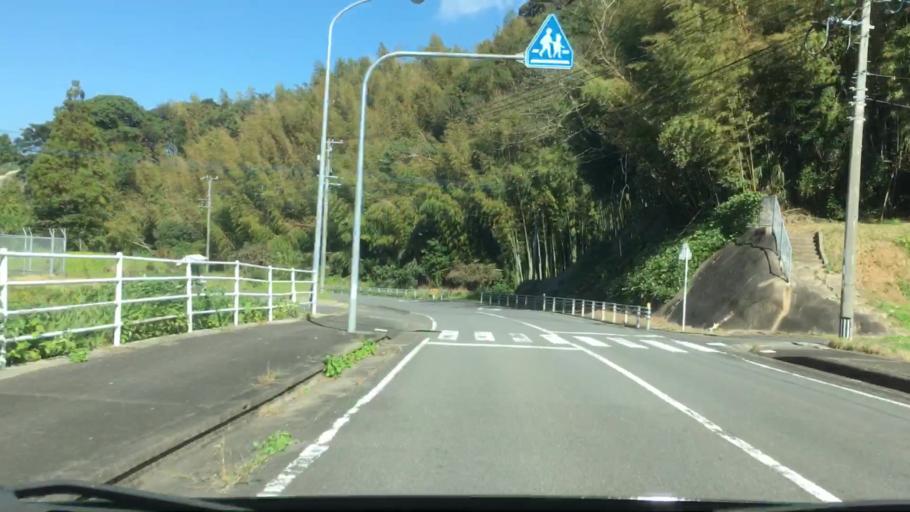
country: JP
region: Nagasaki
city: Sasebo
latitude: 33.0106
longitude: 129.6560
